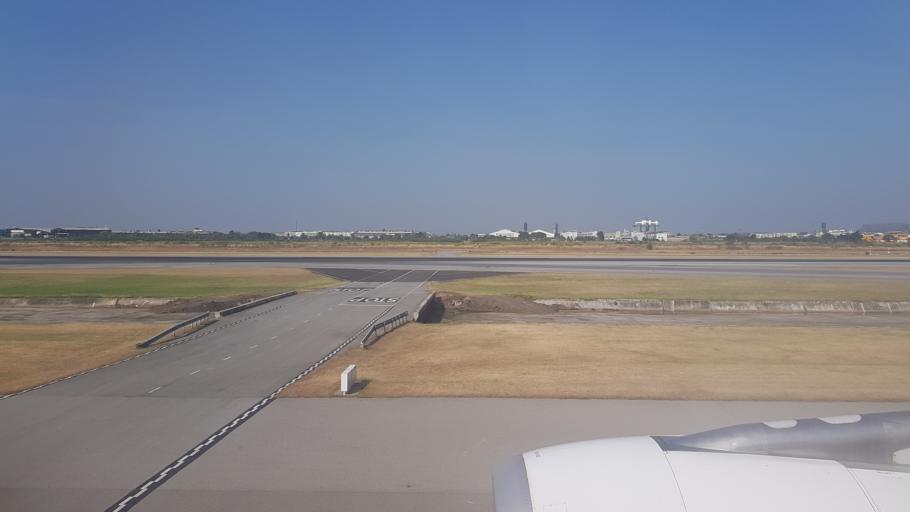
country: TH
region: Bangkok
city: Lat Krabang
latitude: 13.6846
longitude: 100.7401
